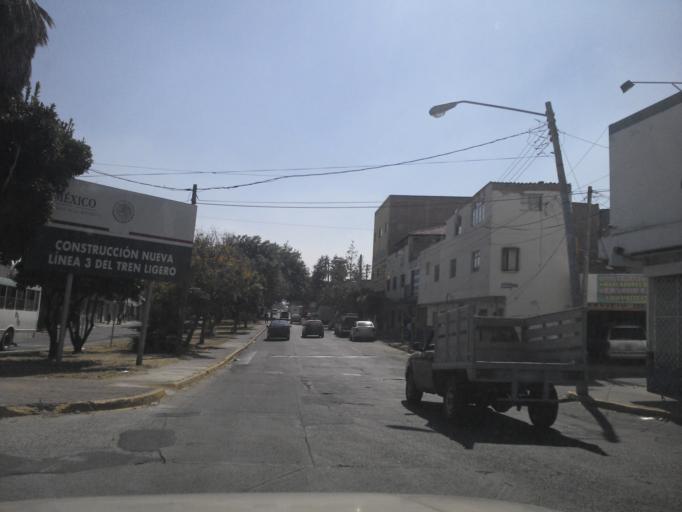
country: MX
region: Jalisco
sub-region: Zapopan
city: Zapopan
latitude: 20.7010
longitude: -103.3577
